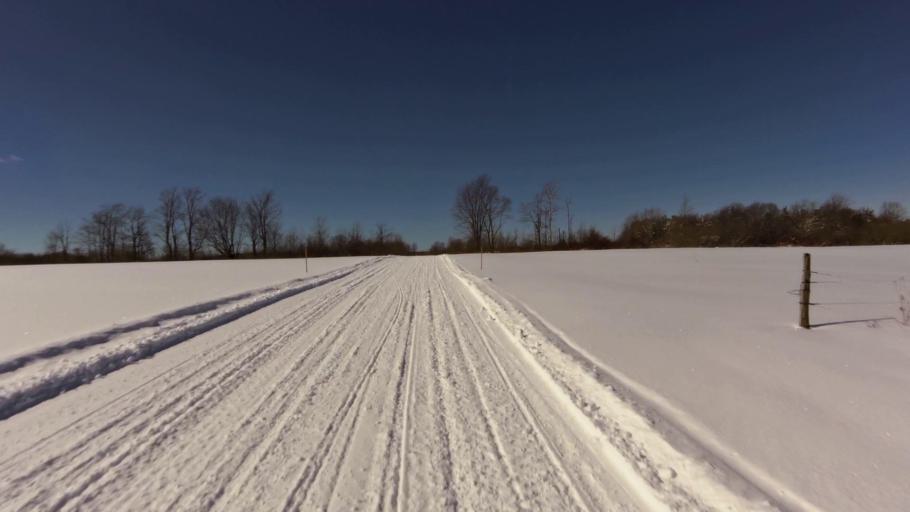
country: US
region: New York
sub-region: Chautauqua County
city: Lakewood
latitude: 42.2257
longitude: -79.3289
